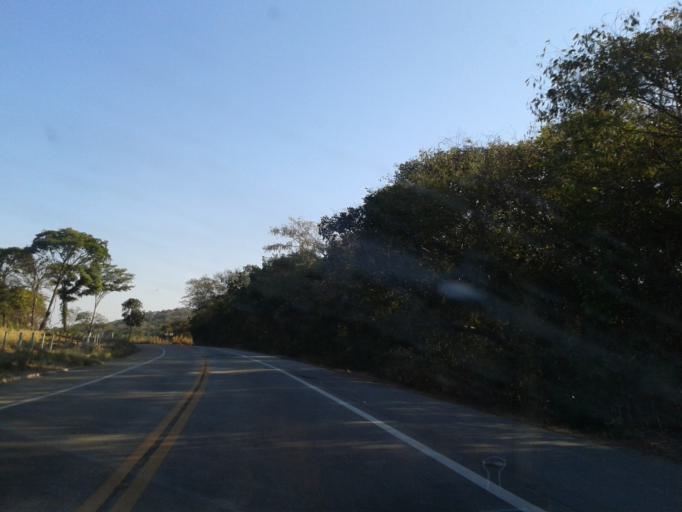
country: BR
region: Goias
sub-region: Itapirapua
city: Itapirapua
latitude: -15.3065
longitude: -50.4438
